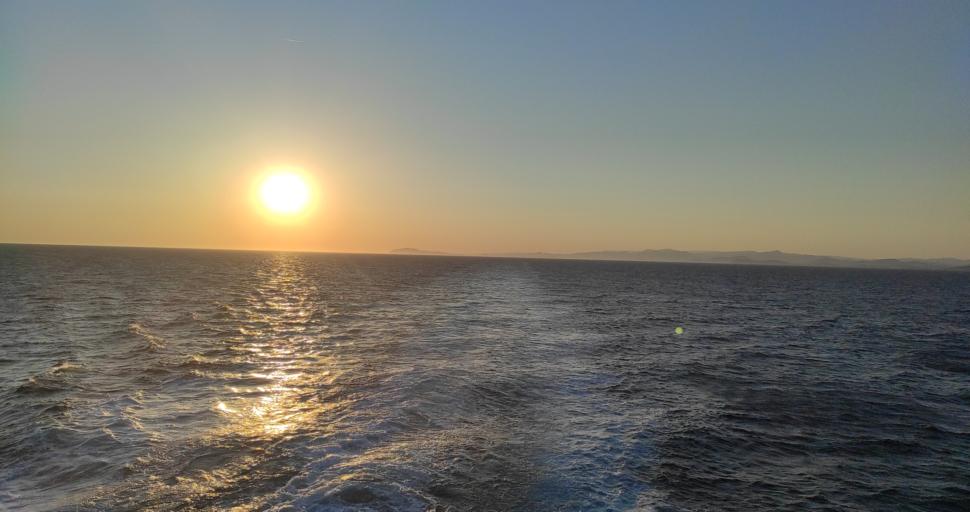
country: FR
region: Provence-Alpes-Cote d'Azur
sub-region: Departement du Var
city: Hyeres
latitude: 42.8802
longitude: 6.2263
